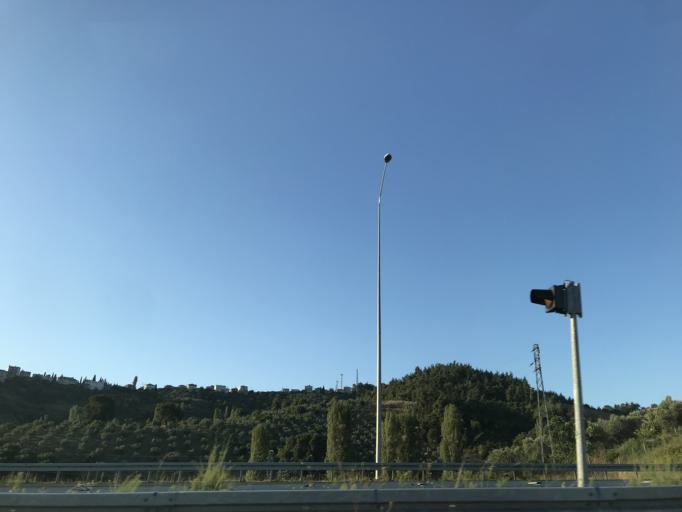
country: TR
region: Bursa
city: Demirtas
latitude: 40.3321
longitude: 29.1130
